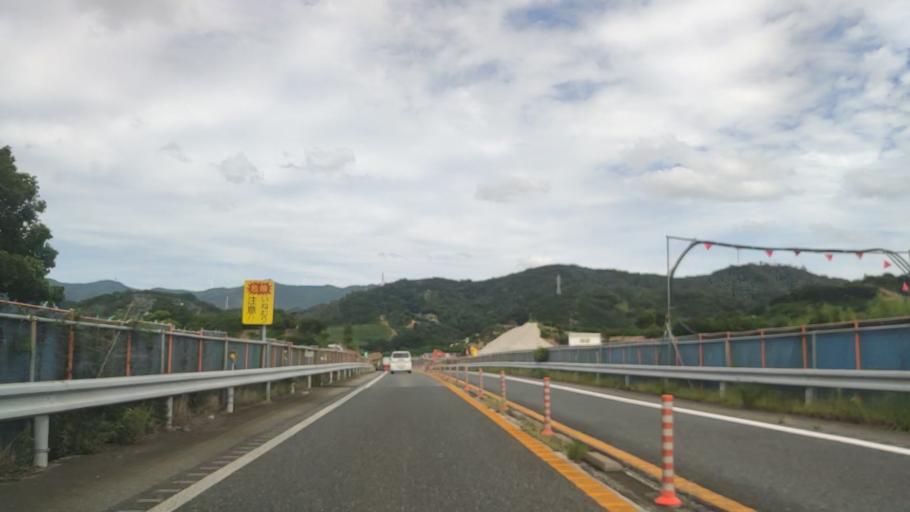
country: JP
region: Wakayama
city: Gobo
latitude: 33.9102
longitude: 135.1943
